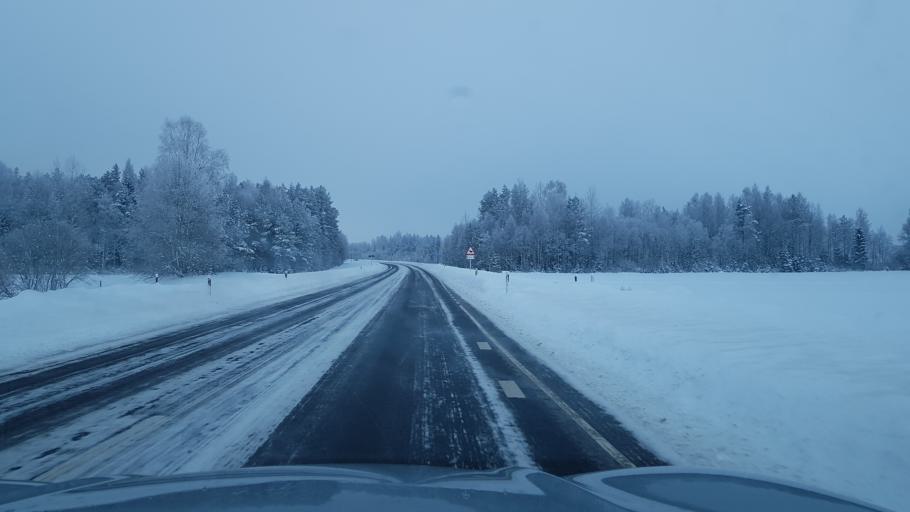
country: EE
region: Ida-Virumaa
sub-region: Johvi vald
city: Johvi
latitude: 59.2245
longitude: 27.3376
